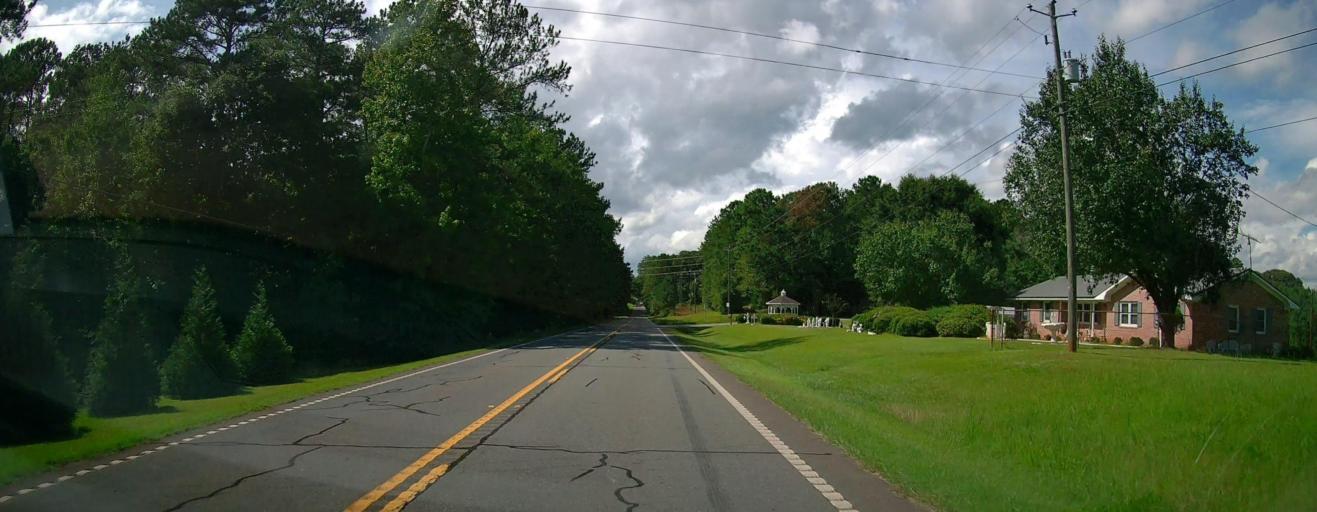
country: US
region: Georgia
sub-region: Talbot County
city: Sardis
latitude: 32.8172
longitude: -84.6038
